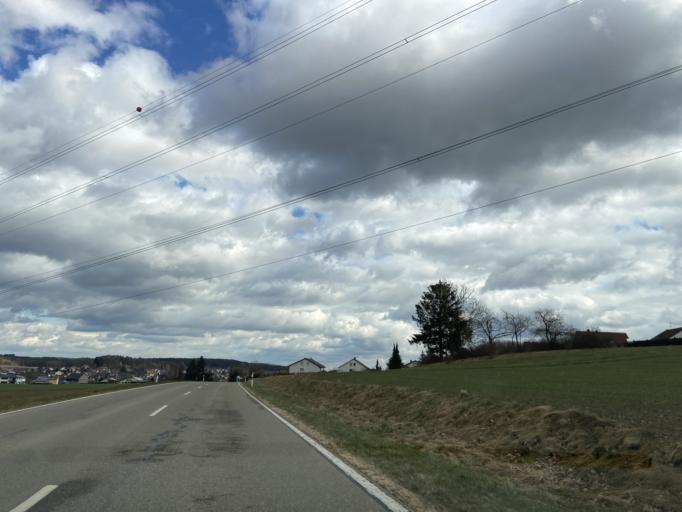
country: DE
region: Baden-Wuerttemberg
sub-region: Tuebingen Region
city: Ostrach
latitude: 47.9541
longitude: 9.3682
